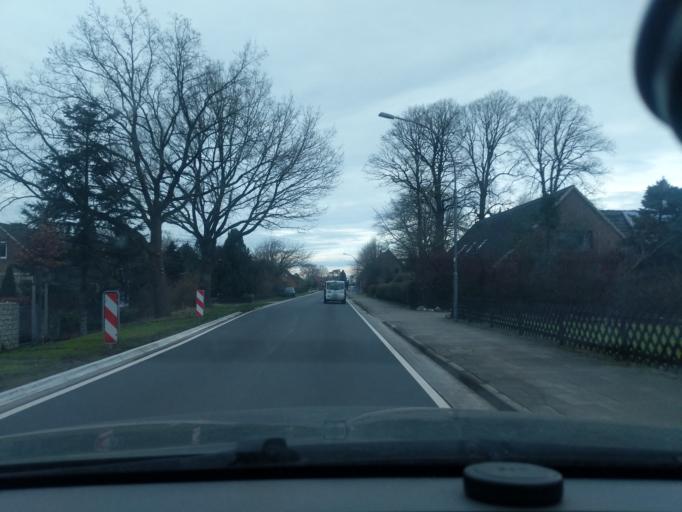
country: DE
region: Lower Saxony
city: Sauensiek
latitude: 53.3826
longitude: 9.5975
